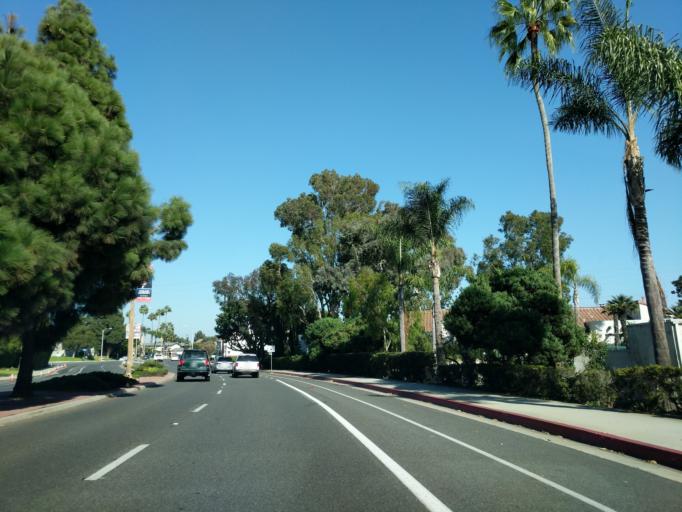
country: US
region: California
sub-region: Orange County
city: Huntington Beach
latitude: 33.6785
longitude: -117.9966
